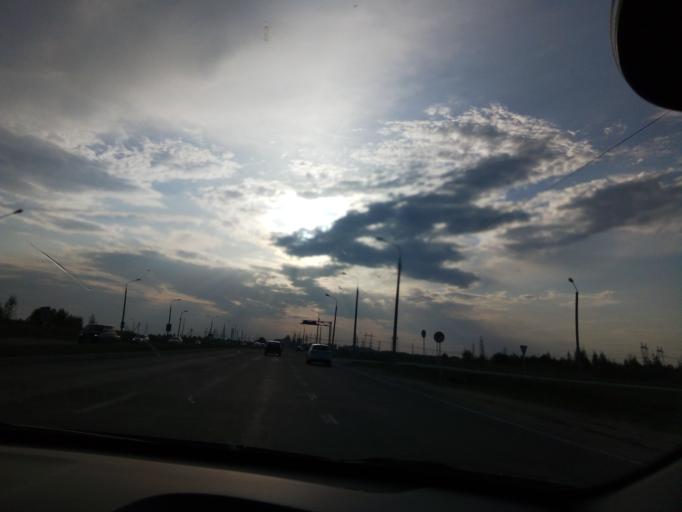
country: RU
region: Chuvashia
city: Novocheboksarsk
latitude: 56.1216
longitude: 47.4330
